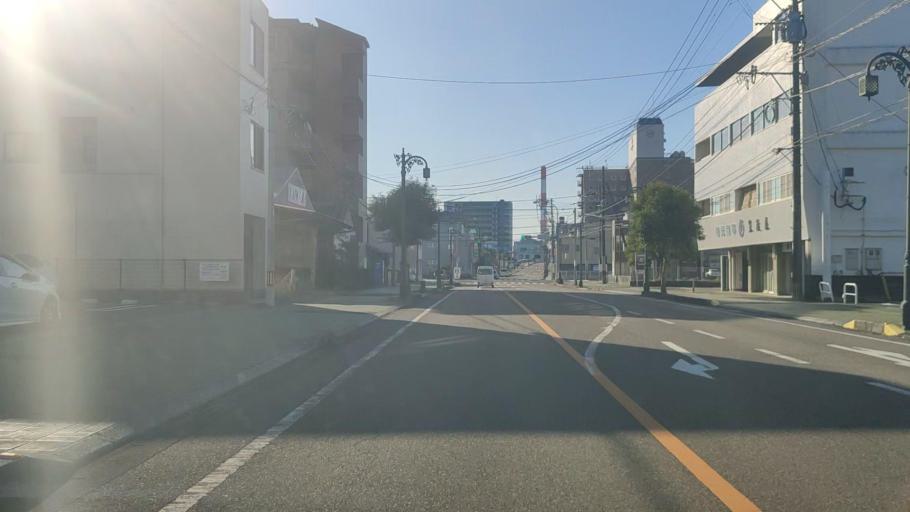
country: JP
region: Miyazaki
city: Nobeoka
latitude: 32.5865
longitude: 131.6712
